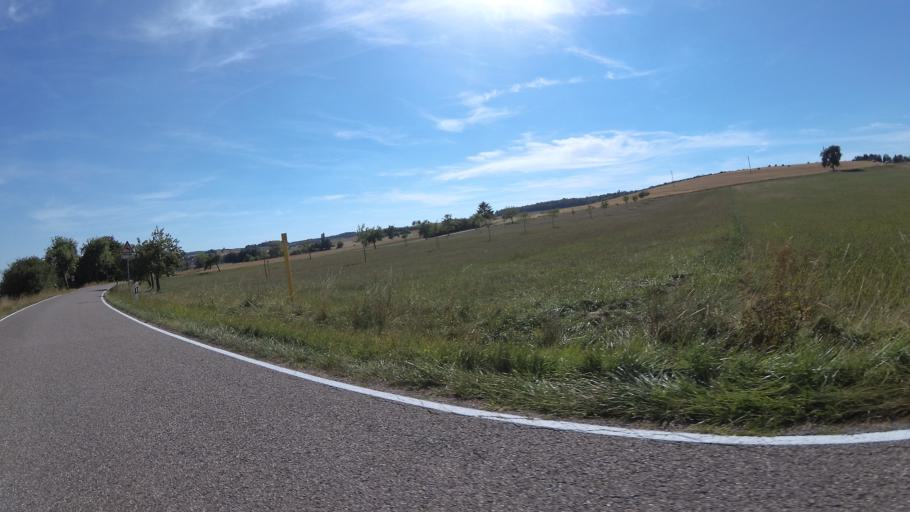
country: DE
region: Saarland
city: Gersheim
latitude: 49.1560
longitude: 7.2778
